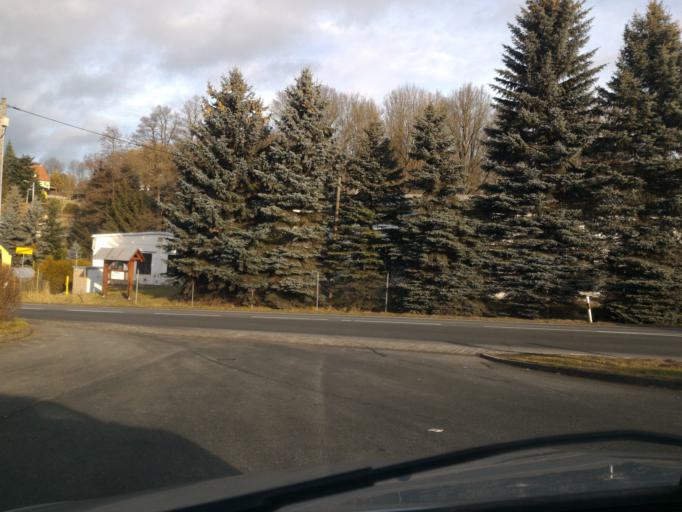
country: DE
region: Saxony
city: Neusalza-Spremberg
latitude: 51.0366
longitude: 14.5437
